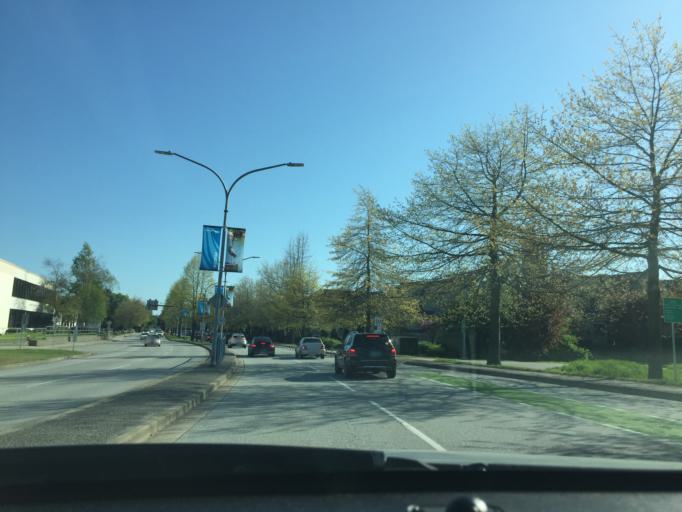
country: CA
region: British Columbia
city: Richmond
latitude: 49.1727
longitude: -123.1587
